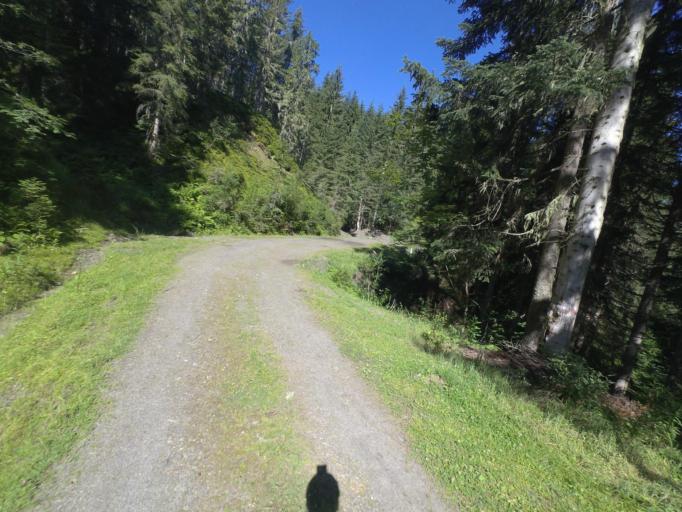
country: AT
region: Salzburg
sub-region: Politischer Bezirk Sankt Johann im Pongau
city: Sankt Veit im Pongau
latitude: 47.3477
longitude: 13.1529
